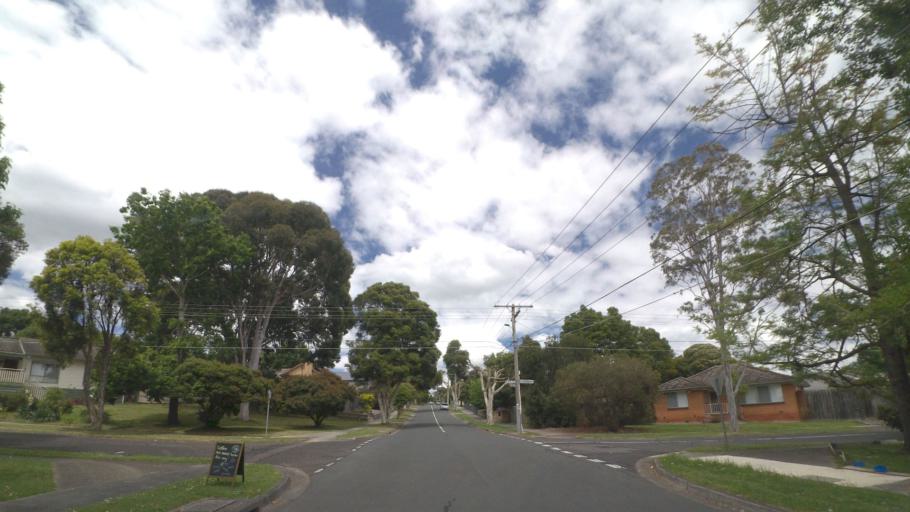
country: AU
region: Victoria
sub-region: Yarra Ranges
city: Kilsyth
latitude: -37.7947
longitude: 145.3087
